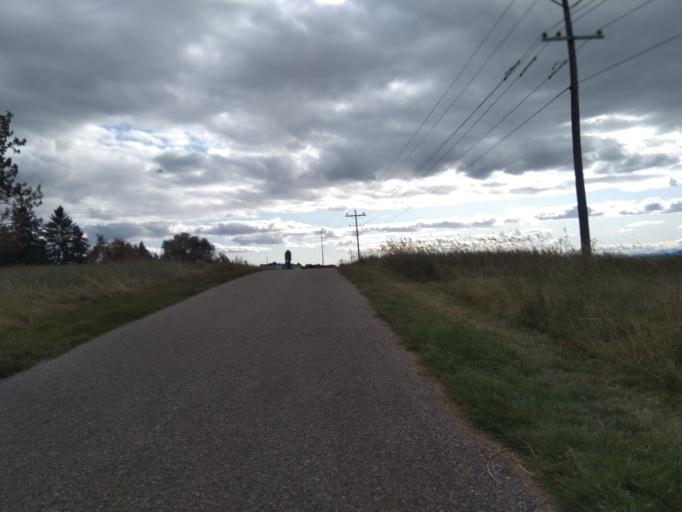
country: CA
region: Alberta
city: Calgary
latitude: 51.0331
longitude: -113.9947
